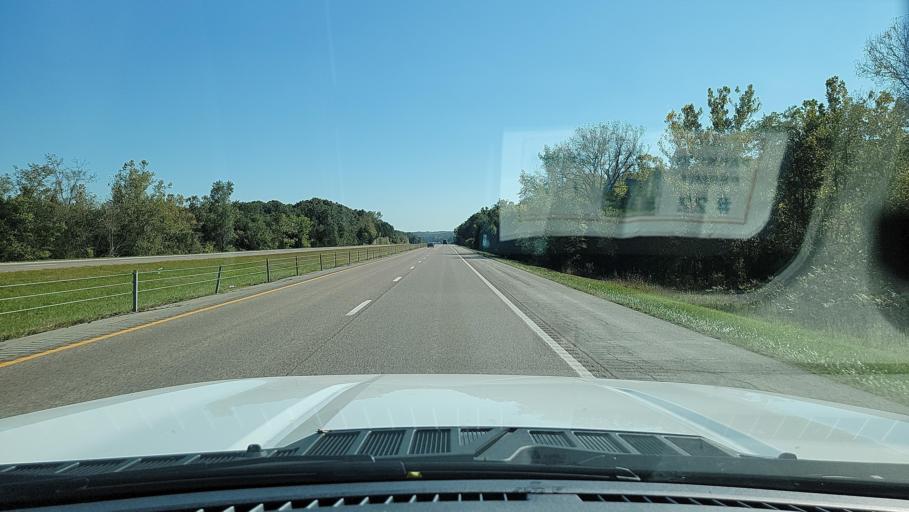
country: US
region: Missouri
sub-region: Jefferson County
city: Crystal City
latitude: 38.1021
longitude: -90.3039
